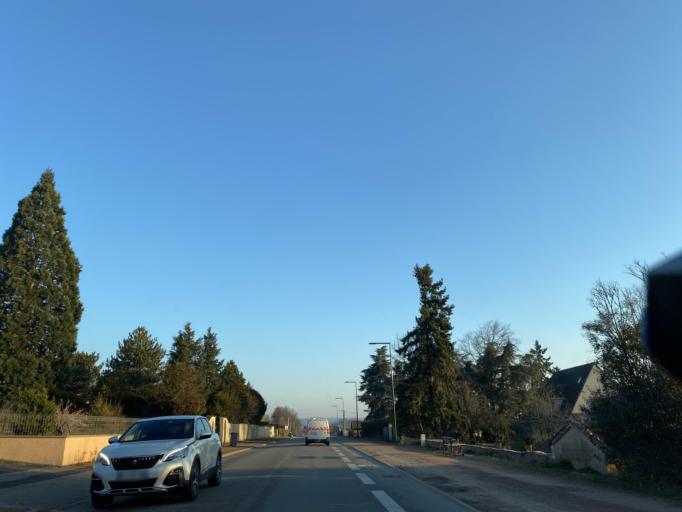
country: FR
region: Rhone-Alpes
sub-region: Departement de la Loire
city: Saint-Germain-Laval
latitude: 45.8346
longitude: 4.0150
